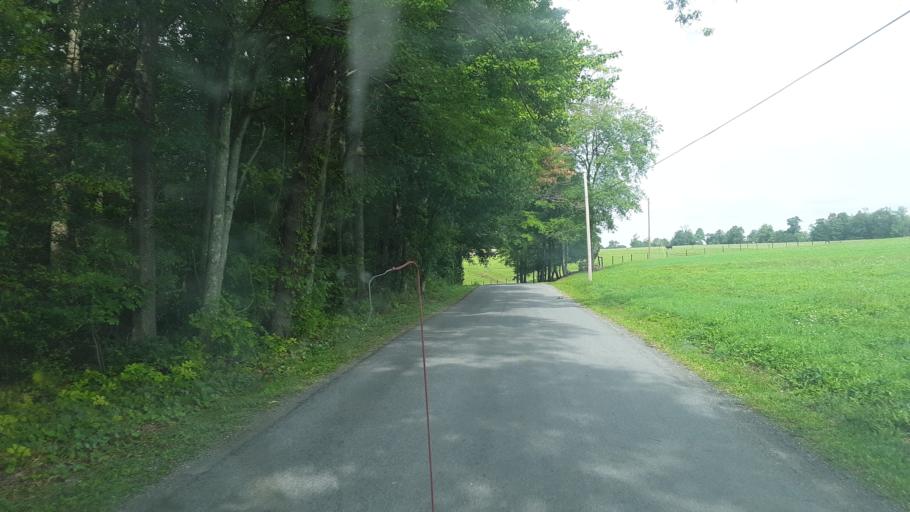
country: US
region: Pennsylvania
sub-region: Jefferson County
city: Punxsutawney
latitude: 40.9380
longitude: -79.0593
